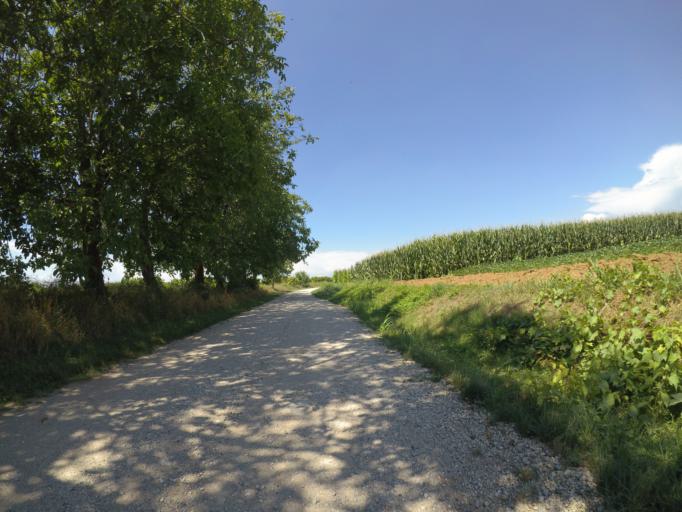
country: IT
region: Friuli Venezia Giulia
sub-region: Provincia di Udine
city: Talmassons
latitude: 45.9358
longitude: 13.1090
